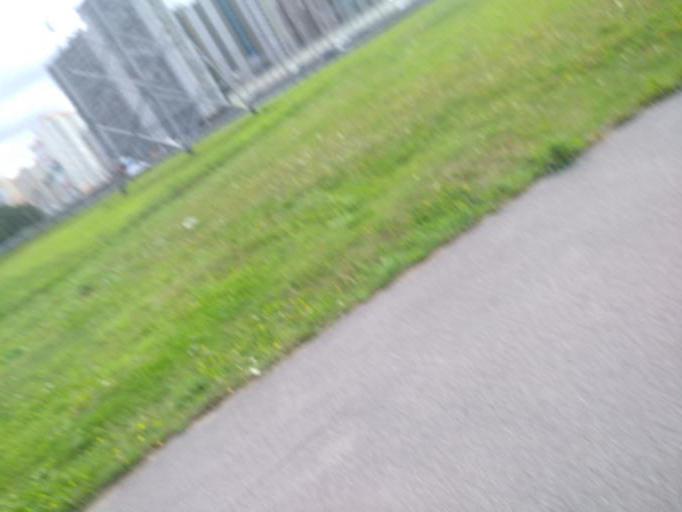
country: RU
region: St.-Petersburg
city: Shushary
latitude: 59.8143
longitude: 30.3785
